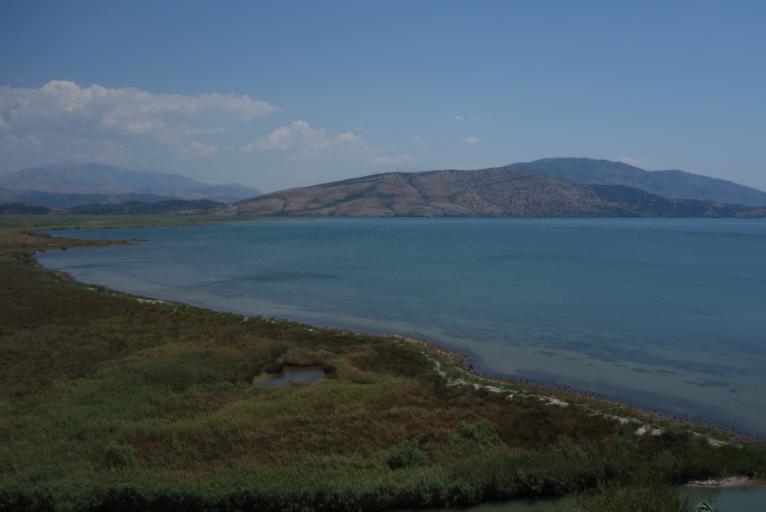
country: AL
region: Vlore
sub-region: Rrethi i Sarandes
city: Sarande
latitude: 39.8139
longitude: 20.0142
